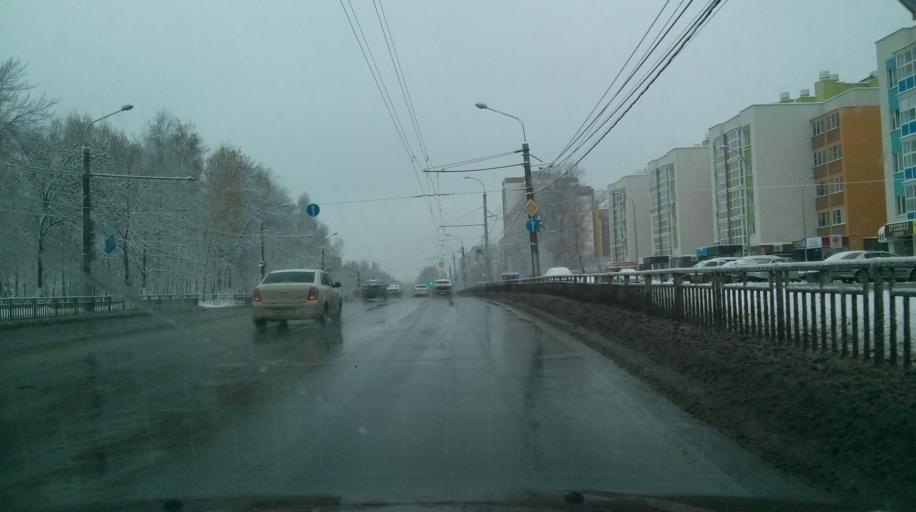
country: RU
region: Nizjnij Novgorod
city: Nizhniy Novgorod
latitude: 56.2385
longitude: 43.9581
